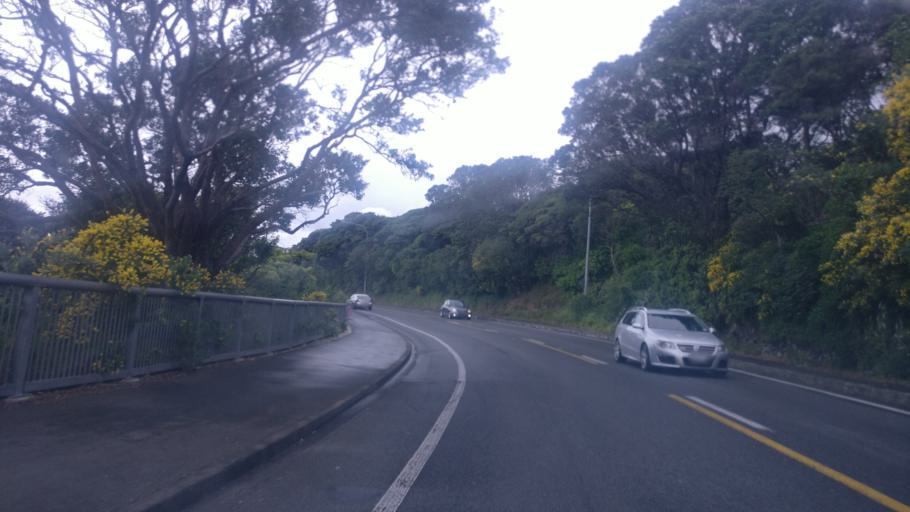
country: NZ
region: Wellington
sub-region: Porirua City
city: Porirua
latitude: -41.0346
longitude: 174.8880
